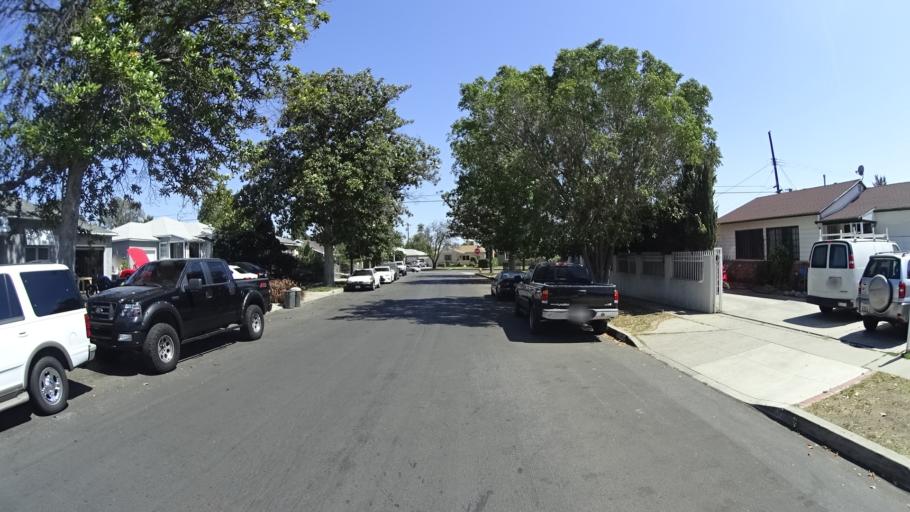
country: US
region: California
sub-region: Los Angeles County
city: Van Nuys
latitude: 34.2180
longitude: -118.4455
